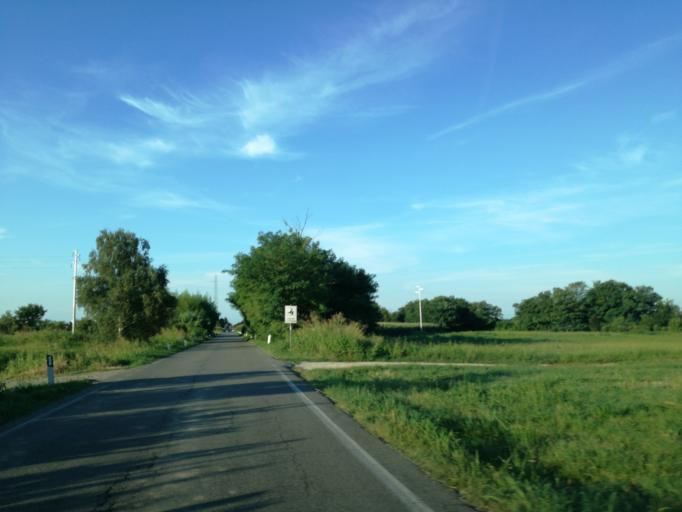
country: IT
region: Lombardy
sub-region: Provincia di Monza e Brianza
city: Sulbiate
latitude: 45.6512
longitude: 9.4306
